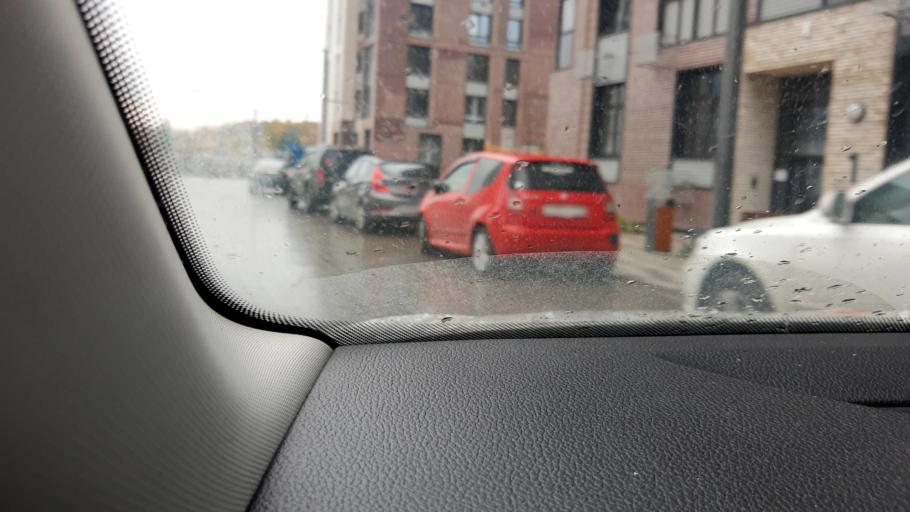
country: RU
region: Moscow
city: Chertanovo Yuzhnoye
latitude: 55.5835
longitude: 37.5818
